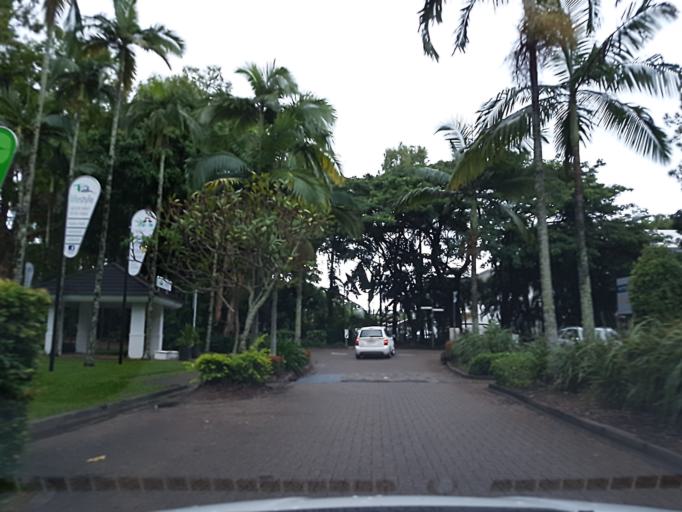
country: AU
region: Queensland
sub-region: Cairns
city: Palm Cove
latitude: -16.7500
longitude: 145.6696
